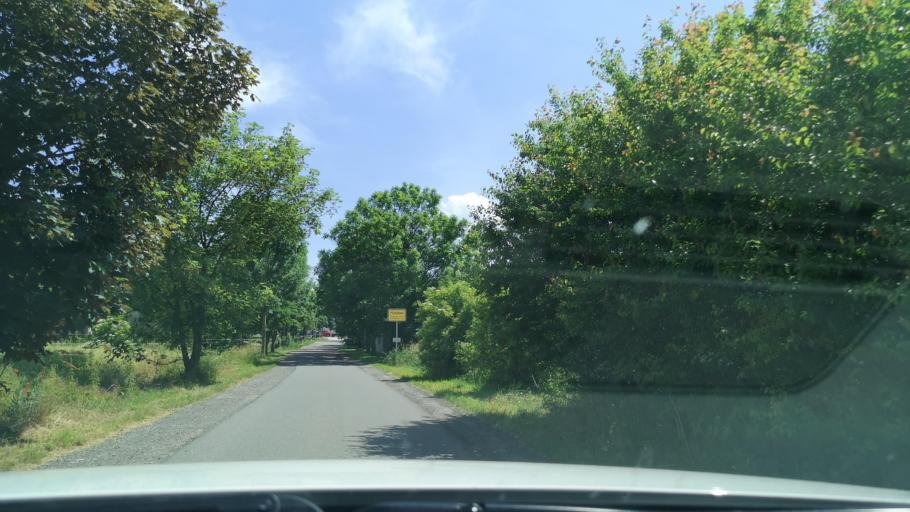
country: DE
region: Thuringia
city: Eberstedt
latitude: 51.0447
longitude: 11.5944
